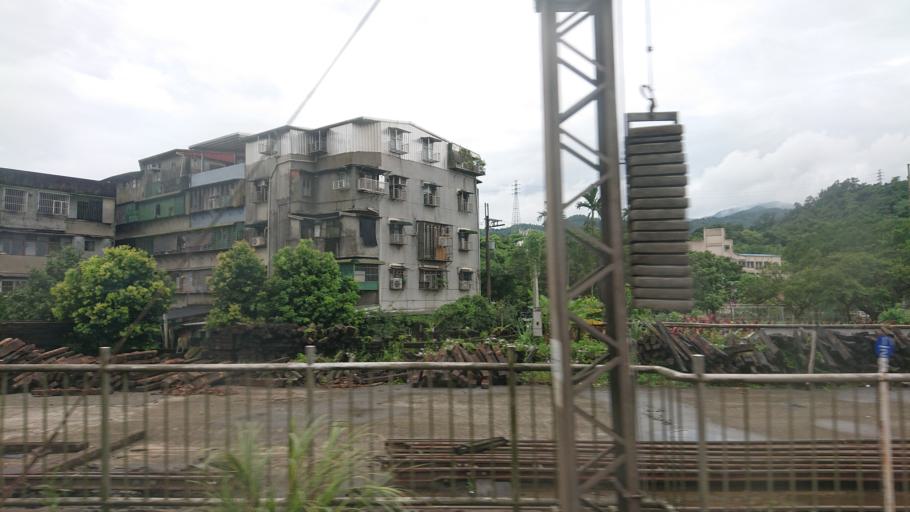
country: TW
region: Taiwan
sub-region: Keelung
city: Keelung
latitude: 25.0959
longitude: 121.7181
